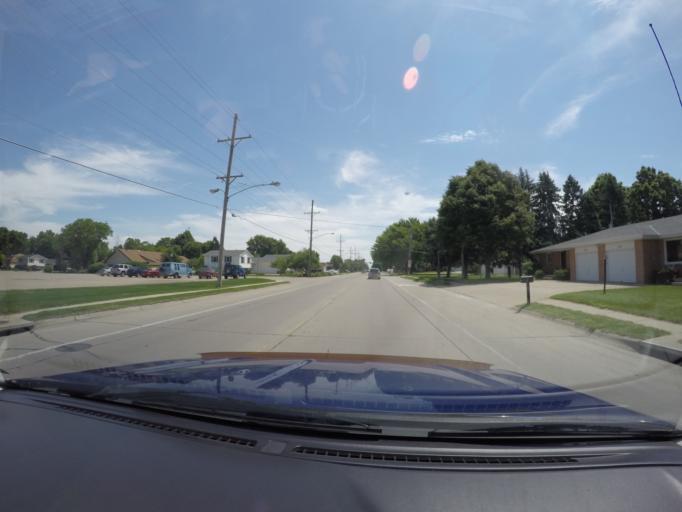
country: US
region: Nebraska
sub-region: Hall County
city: Grand Island
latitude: 40.9023
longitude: -98.3661
